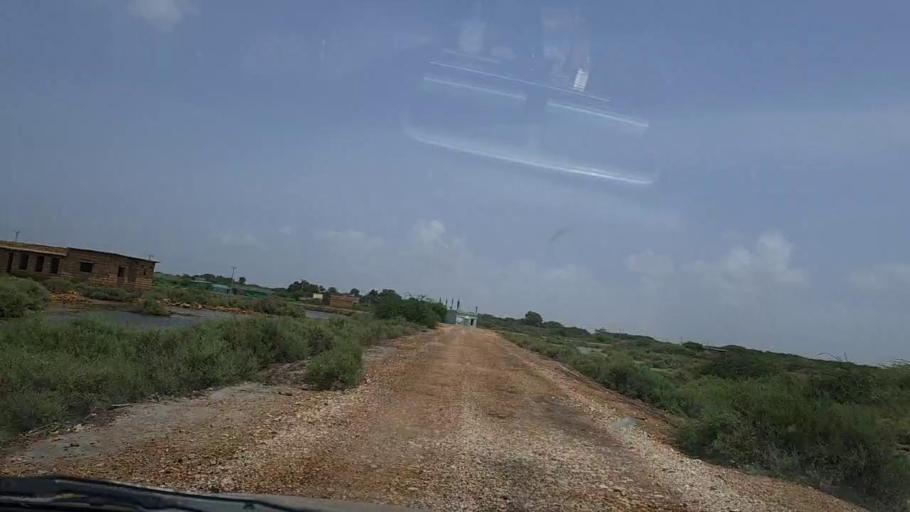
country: PK
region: Sindh
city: Keti Bandar
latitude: 24.1515
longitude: 67.5329
